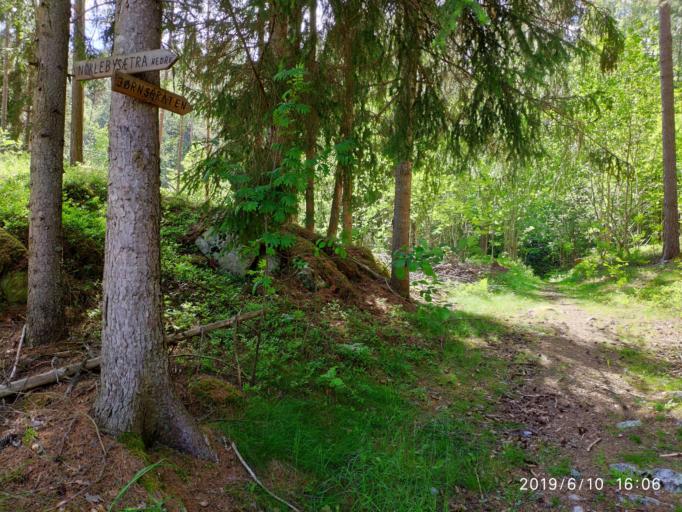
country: NO
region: Oppland
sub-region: Jevnaker
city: Jevnaker
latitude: 60.2497
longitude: 10.3660
